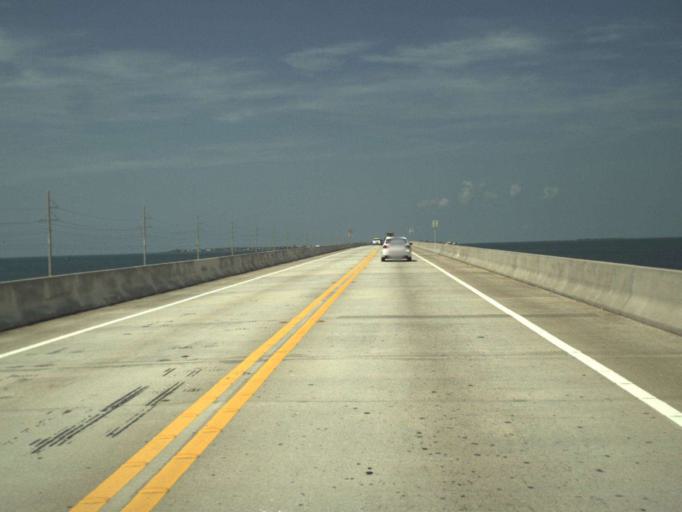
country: US
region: Florida
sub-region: Monroe County
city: Marathon
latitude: 24.8024
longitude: -80.8529
